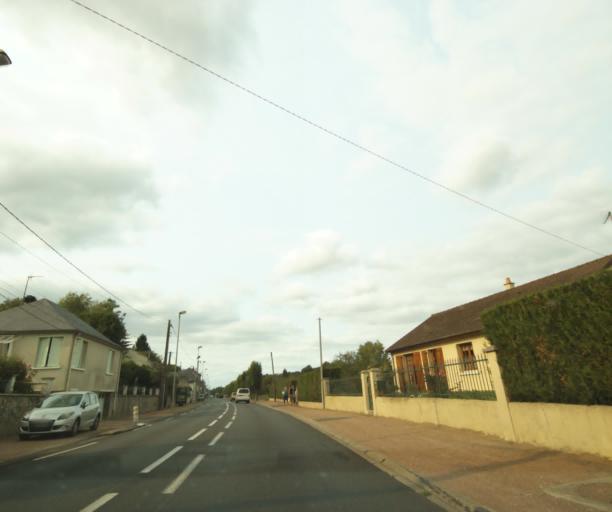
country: FR
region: Centre
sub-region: Departement d'Indre-et-Loire
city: Loches
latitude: 47.1452
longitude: 1.0011
